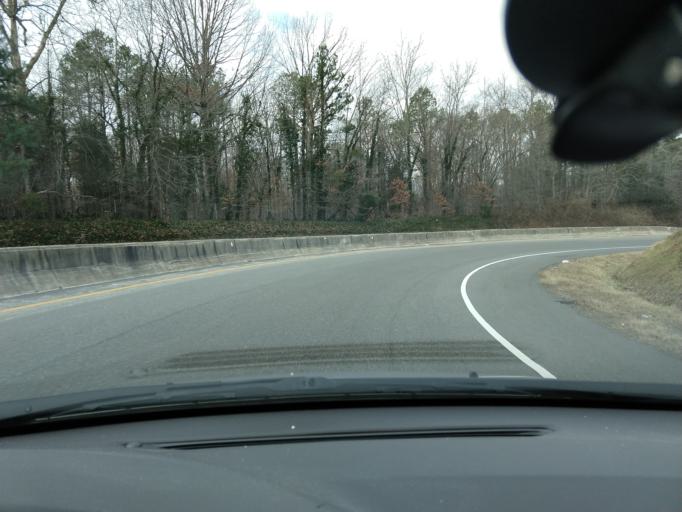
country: US
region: Virginia
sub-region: Chesterfield County
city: Bensley
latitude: 37.4427
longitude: -77.4408
